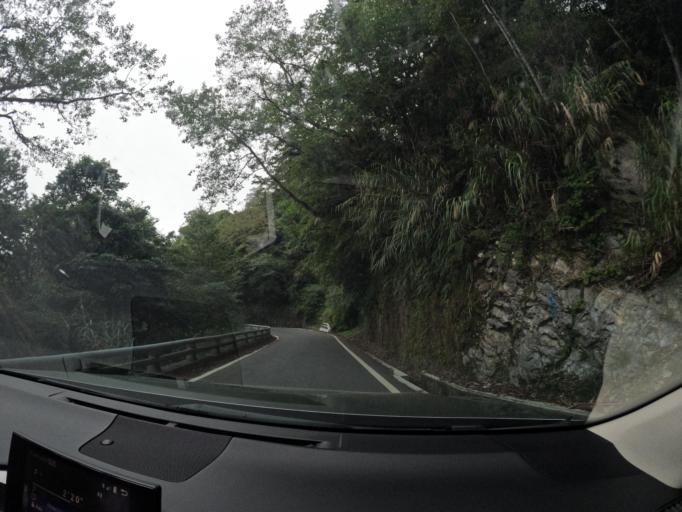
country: TW
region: Taiwan
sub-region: Taitung
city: Taitung
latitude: 23.2418
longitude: 120.9846
